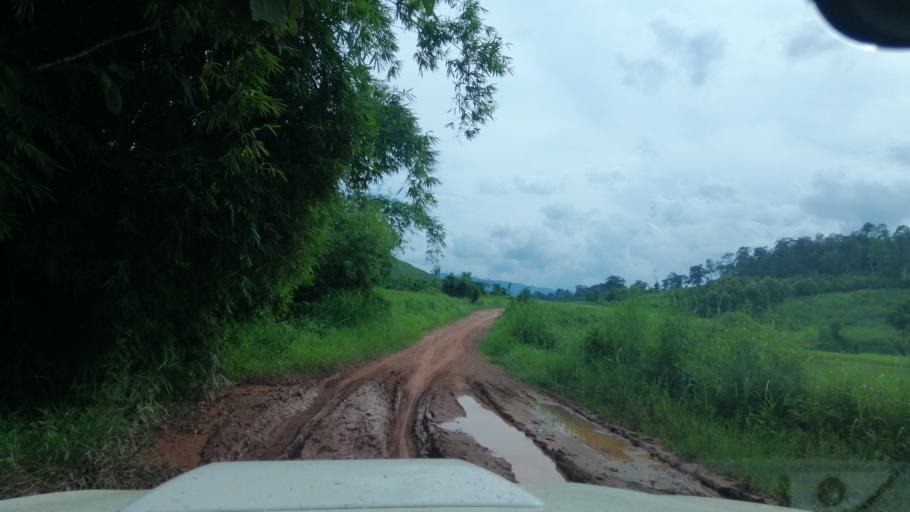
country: TH
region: Nan
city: Mae Charim
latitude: 18.7783
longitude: 101.3190
